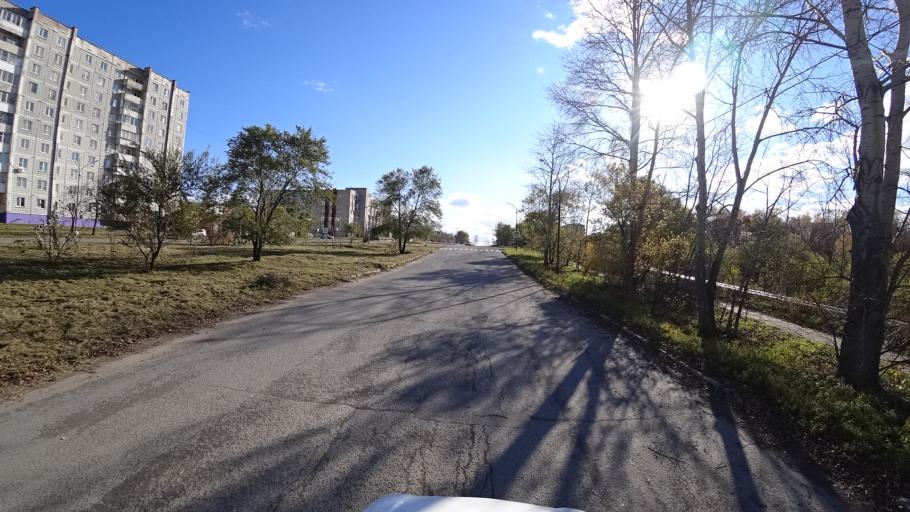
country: RU
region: Khabarovsk Krai
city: Amursk
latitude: 50.2446
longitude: 136.9150
